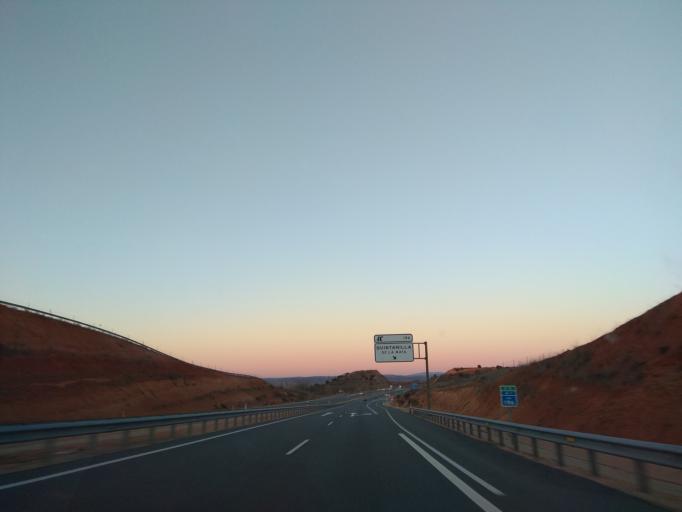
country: ES
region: Castille and Leon
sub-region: Provincia de Burgos
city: Quintanilla de la Mata
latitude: 41.9806
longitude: -3.7725
